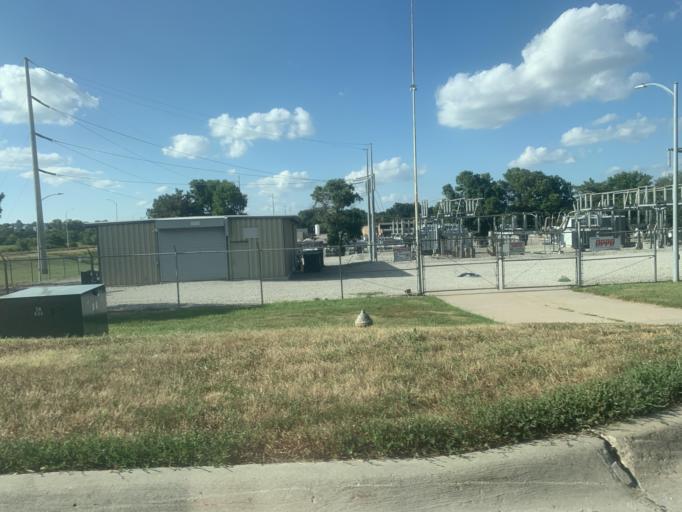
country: US
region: Nebraska
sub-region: Sarpy County
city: Chalco
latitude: 41.1764
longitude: -96.1382
